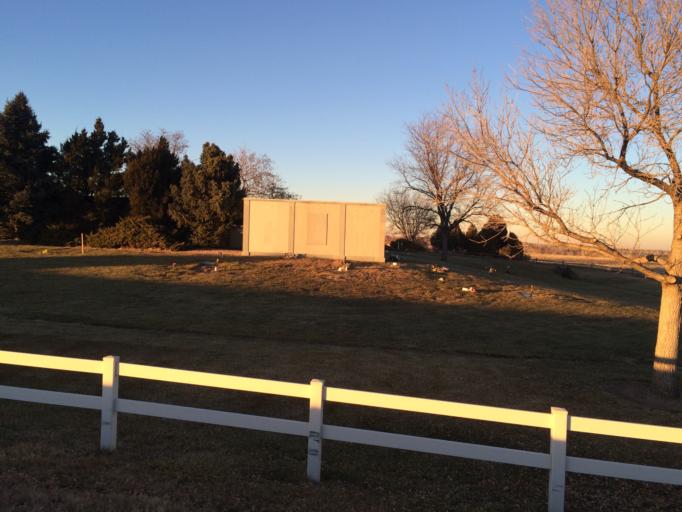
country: US
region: Colorado
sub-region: Boulder County
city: Louisville
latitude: 39.9726
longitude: -105.1136
